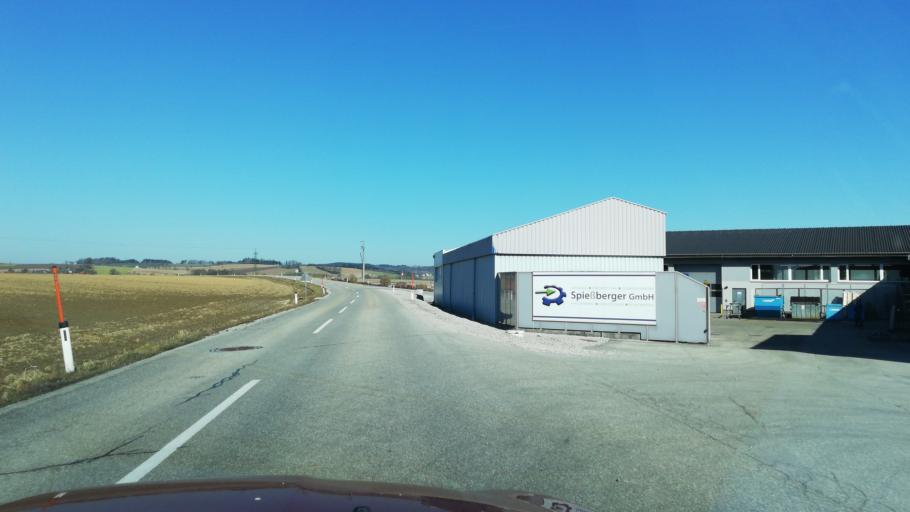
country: AT
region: Upper Austria
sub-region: Politischer Bezirk Vocklabruck
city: Schlatt
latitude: 48.0732
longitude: 13.8106
